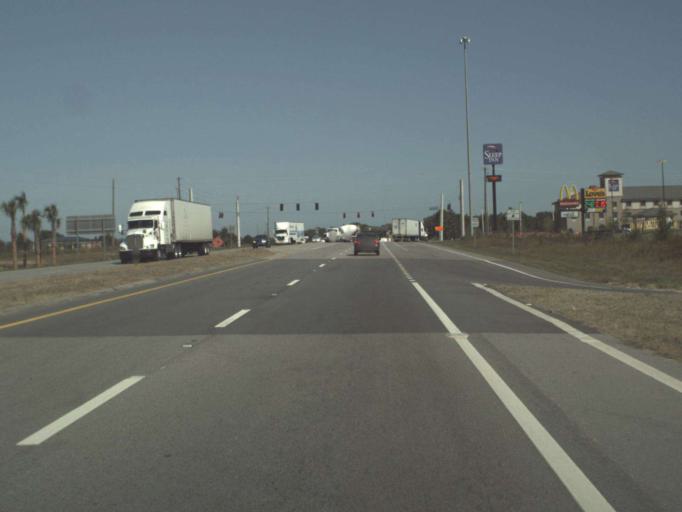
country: US
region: Florida
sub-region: Okaloosa County
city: Crestview
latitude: 30.7335
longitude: -86.3506
